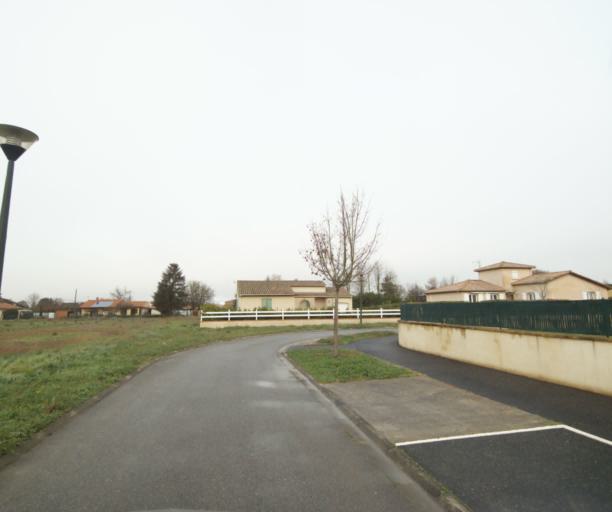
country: FR
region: Midi-Pyrenees
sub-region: Departement de la Haute-Garonne
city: Villemur-sur-Tarn
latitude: 43.8558
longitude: 1.4793
